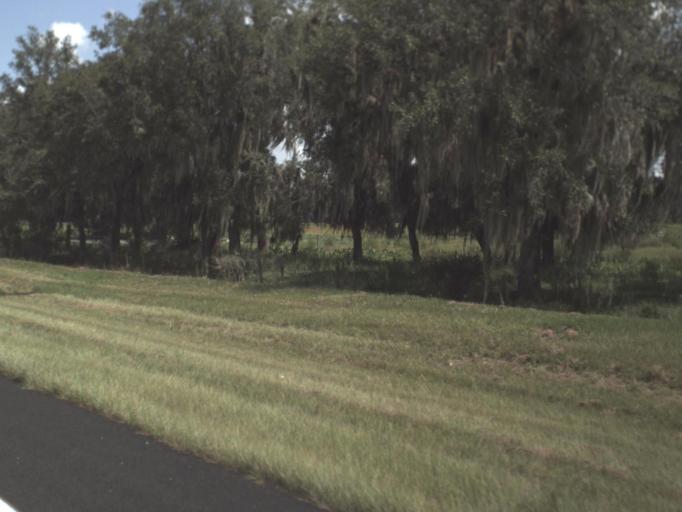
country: US
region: Florida
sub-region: Hardee County
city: Zolfo Springs
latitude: 27.4705
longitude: -81.7975
